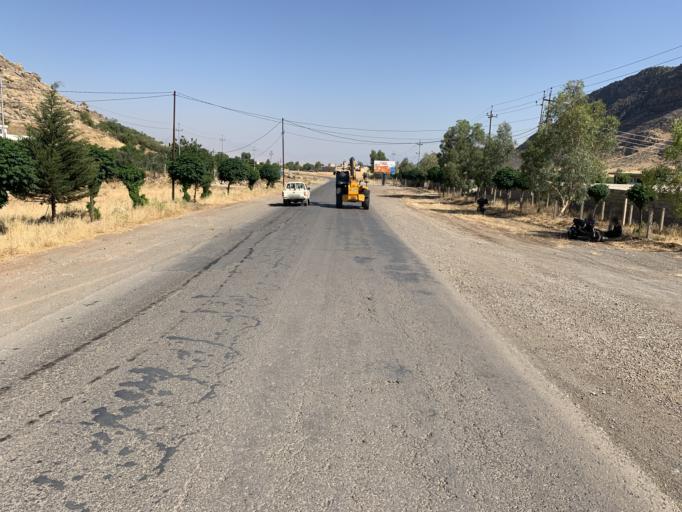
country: IQ
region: As Sulaymaniyah
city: Raniye
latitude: 36.2687
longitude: 44.8380
